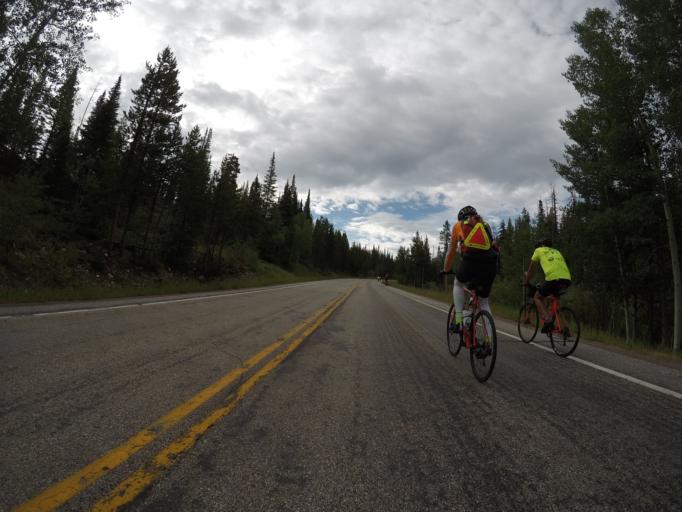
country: US
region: Wyoming
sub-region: Carbon County
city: Saratoga
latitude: 41.3368
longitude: -106.5223
